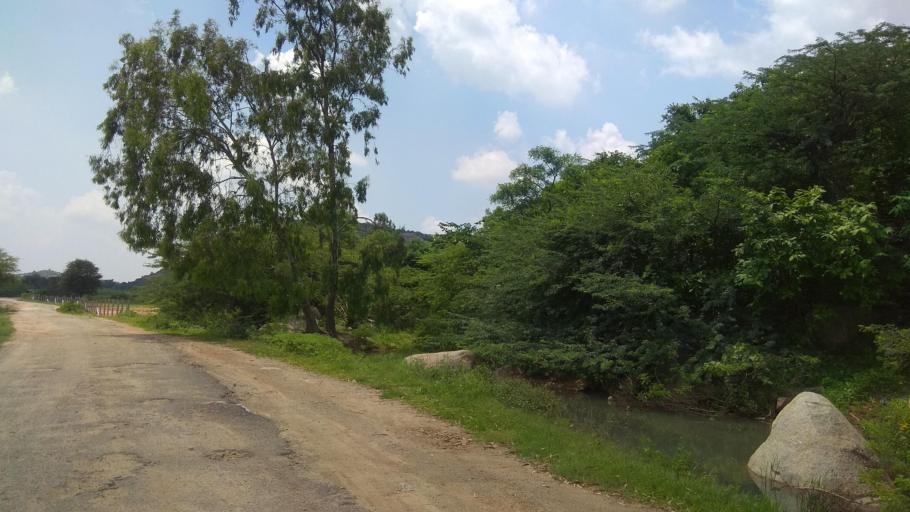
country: IN
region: Telangana
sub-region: Mahbubnagar
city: Farrukhnagar
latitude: 16.8856
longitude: 78.5166
